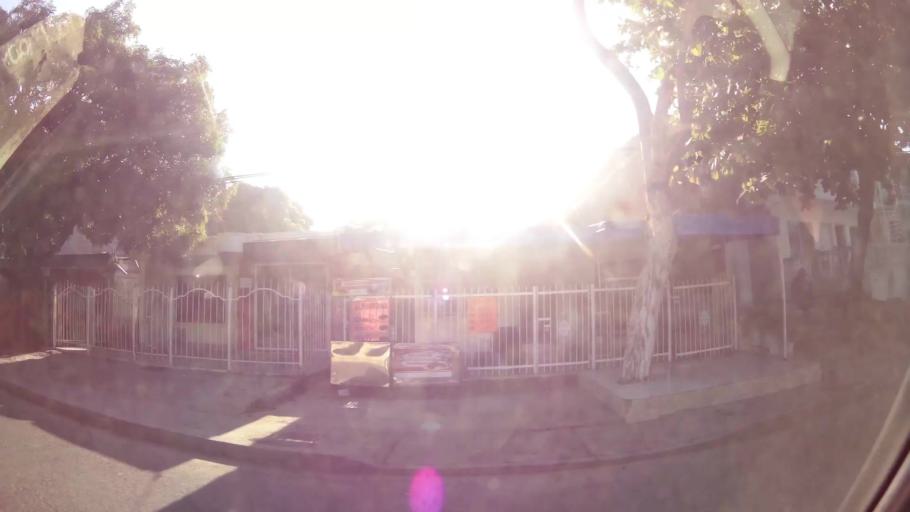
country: CO
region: Bolivar
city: Cartagena
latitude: 10.3983
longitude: -75.4993
